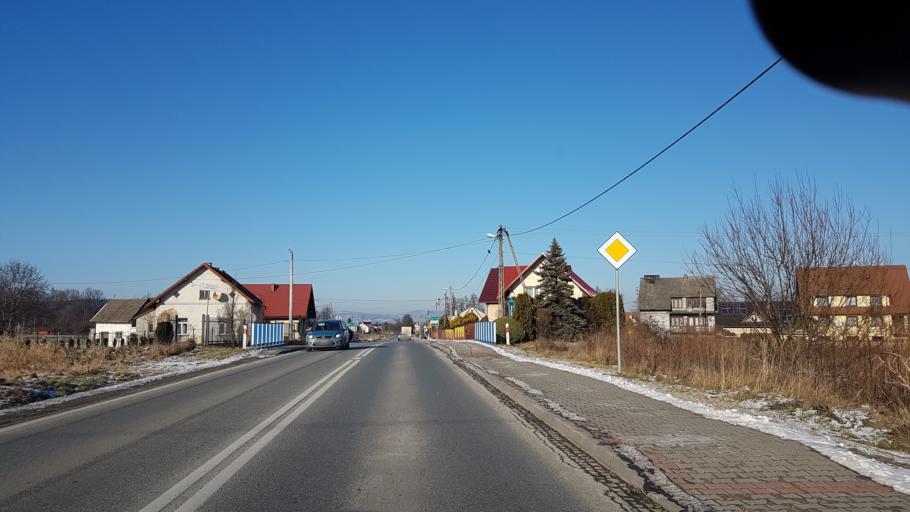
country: PL
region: Lesser Poland Voivodeship
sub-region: Powiat nowosadecki
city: Stary Sacz
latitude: 49.5350
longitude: 20.6477
